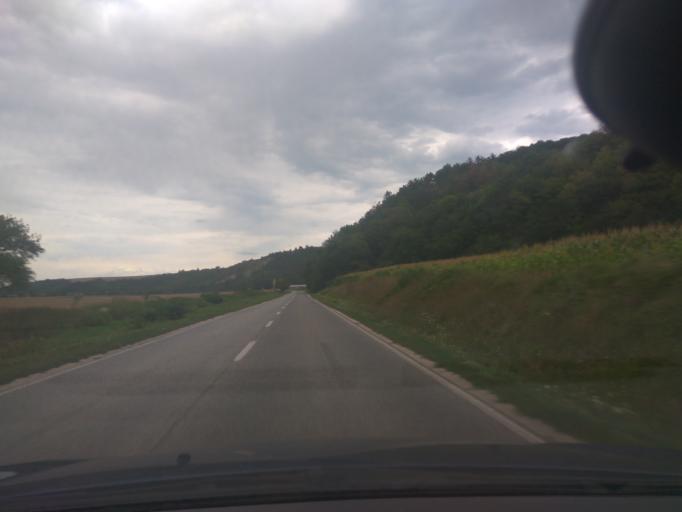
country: SK
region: Trnavsky
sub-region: Okres Trnava
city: Piestany
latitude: 48.6148
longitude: 17.8673
